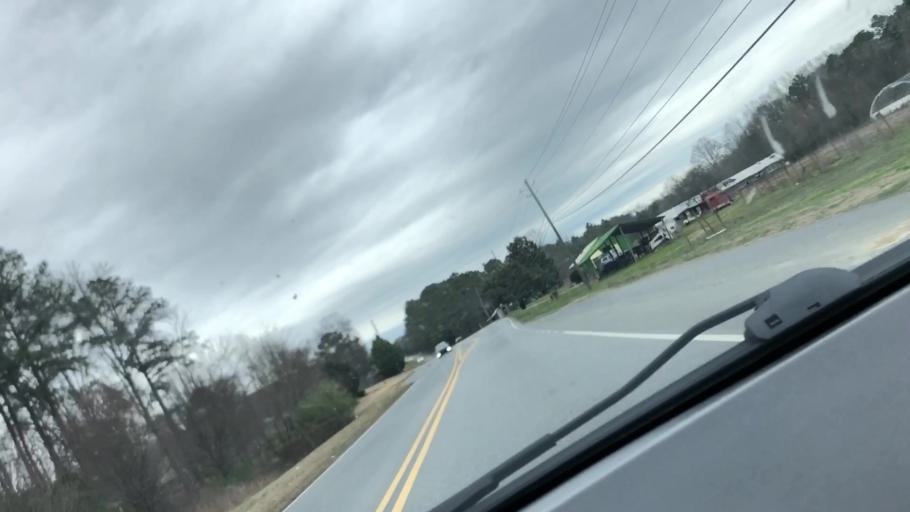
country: US
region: Georgia
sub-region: Bartow County
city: Cartersville
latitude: 34.1865
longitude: -84.8306
